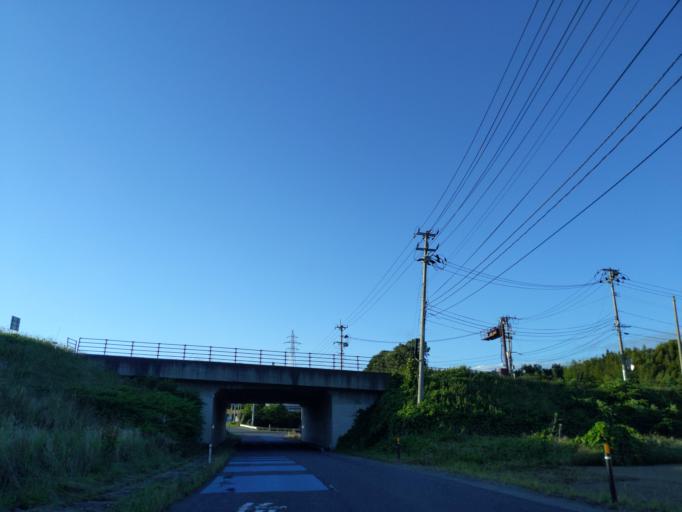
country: JP
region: Fukushima
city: Koriyama
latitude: 37.3938
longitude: 140.4120
